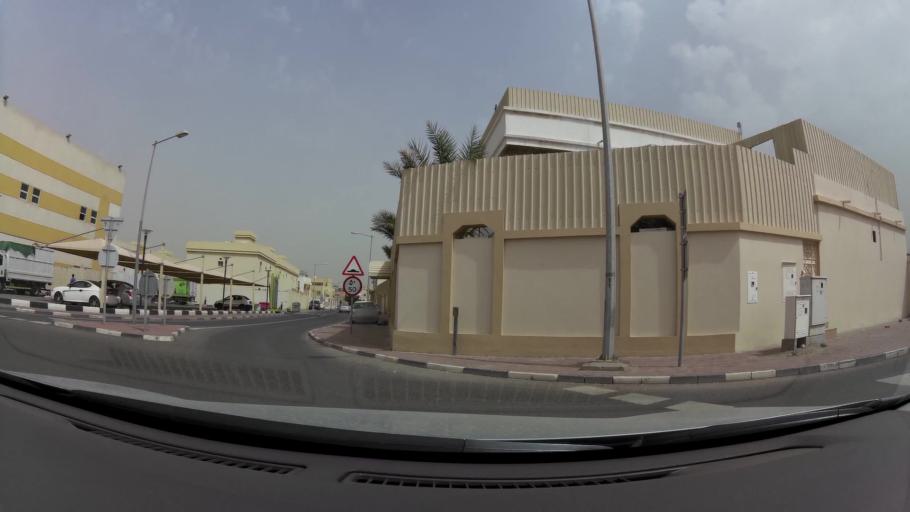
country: QA
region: Baladiyat ad Dawhah
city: Doha
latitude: 25.2586
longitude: 51.5276
